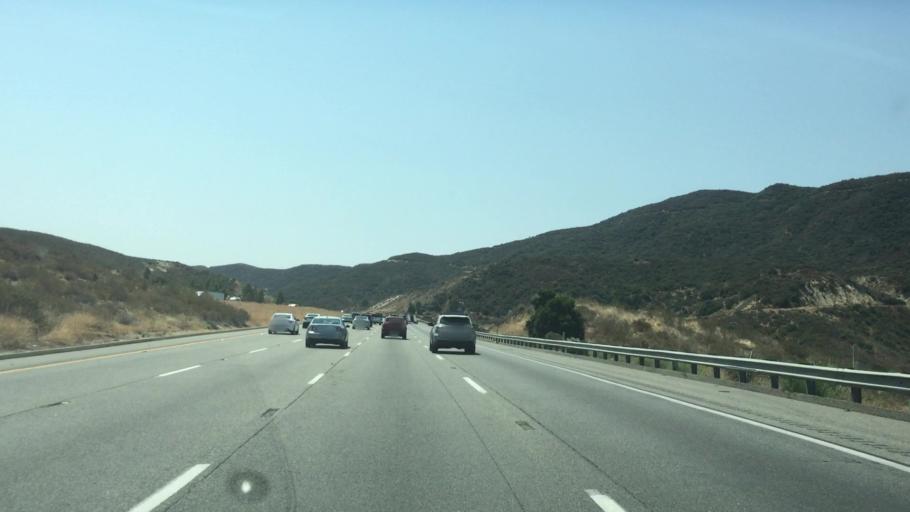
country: US
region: California
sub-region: Los Angeles County
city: Castaic
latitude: 34.5949
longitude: -118.7123
